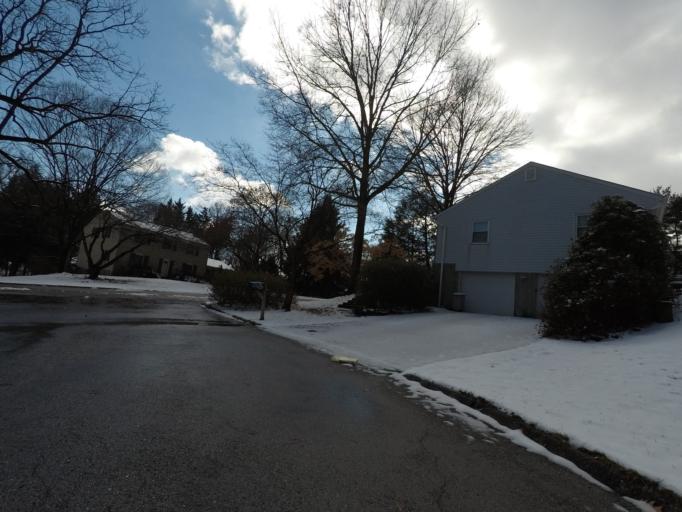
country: US
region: Maryland
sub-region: Howard County
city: Columbia
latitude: 39.2685
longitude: -76.8391
